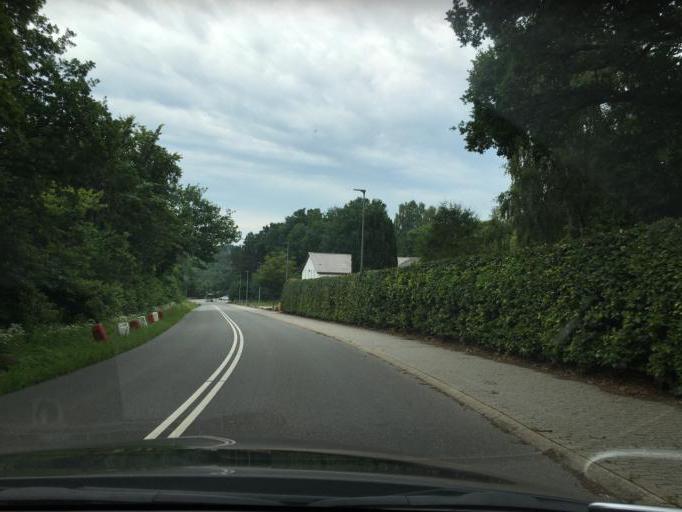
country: DK
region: South Denmark
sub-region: Kolding Kommune
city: Kolding
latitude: 55.5706
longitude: 9.4889
